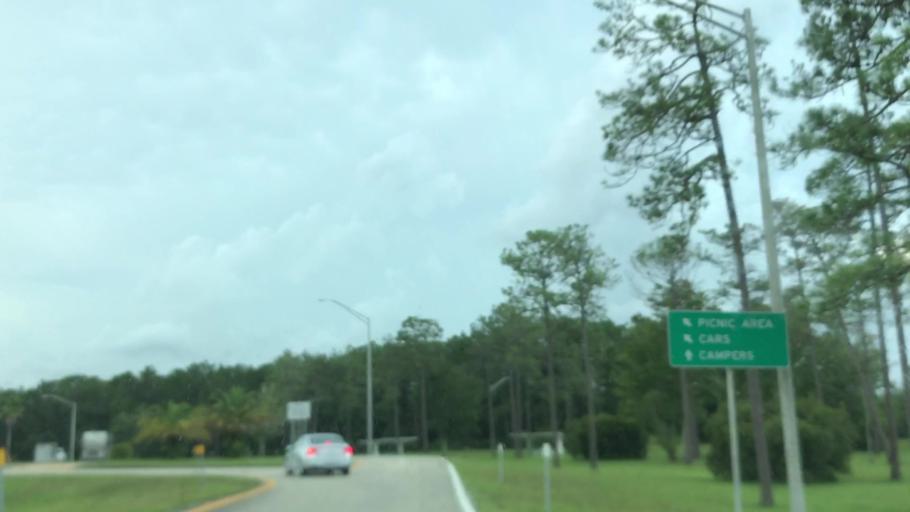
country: US
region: Florida
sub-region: Saint Johns County
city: Saint Augustine Shores
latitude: 29.7010
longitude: -81.3266
